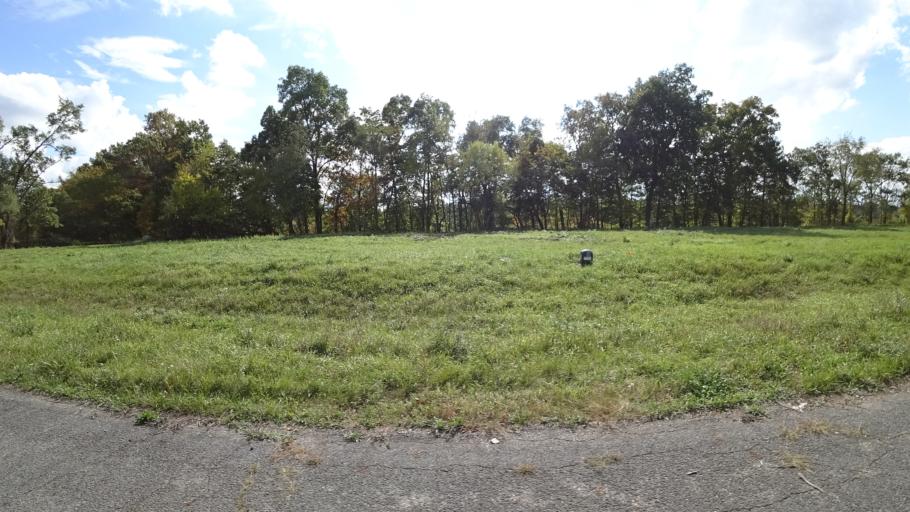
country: US
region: Michigan
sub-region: Saint Joseph County
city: Three Rivers
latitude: 41.9437
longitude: -85.6078
